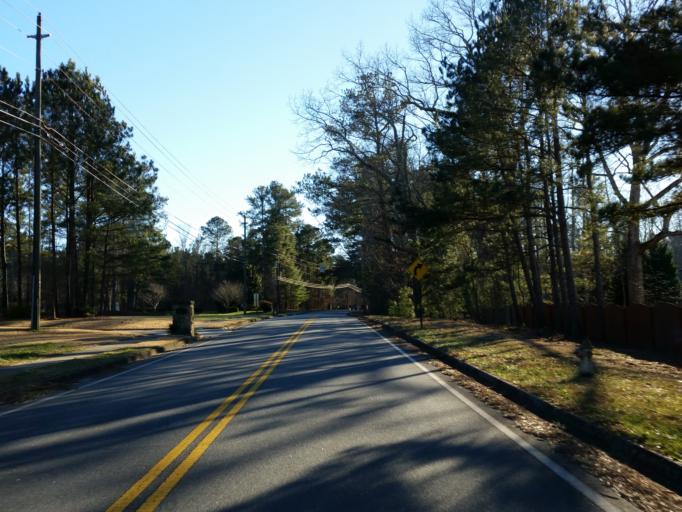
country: US
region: Georgia
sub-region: Cobb County
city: Kennesaw
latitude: 33.9745
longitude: -84.6914
